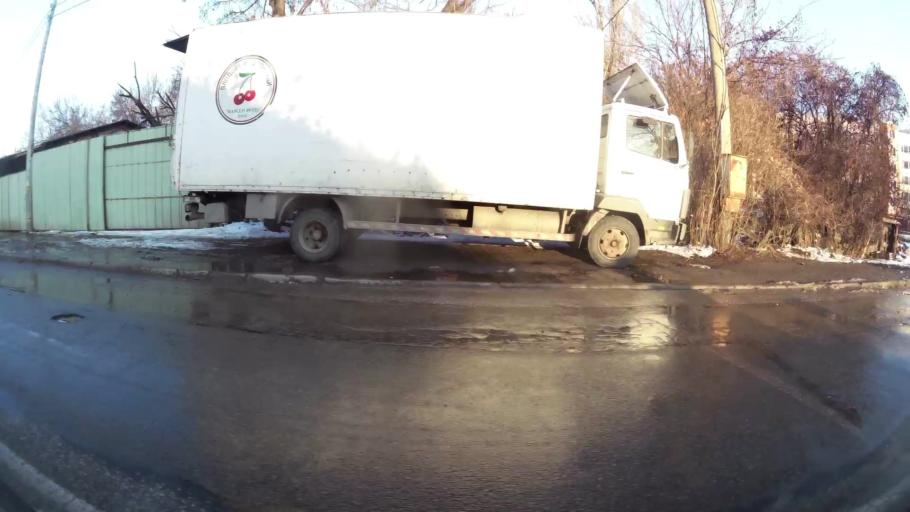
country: BG
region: Sofia-Capital
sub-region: Stolichna Obshtina
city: Sofia
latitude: 42.6783
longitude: 23.3786
